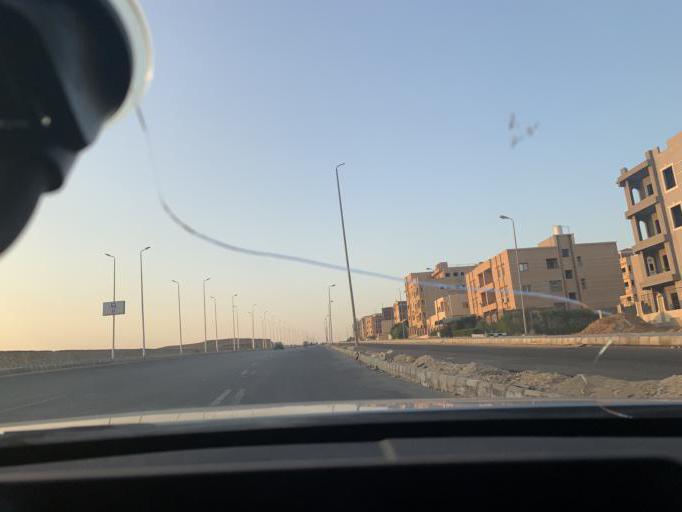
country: EG
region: Muhafazat al Qahirah
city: Halwan
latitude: 29.9787
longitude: 31.4690
